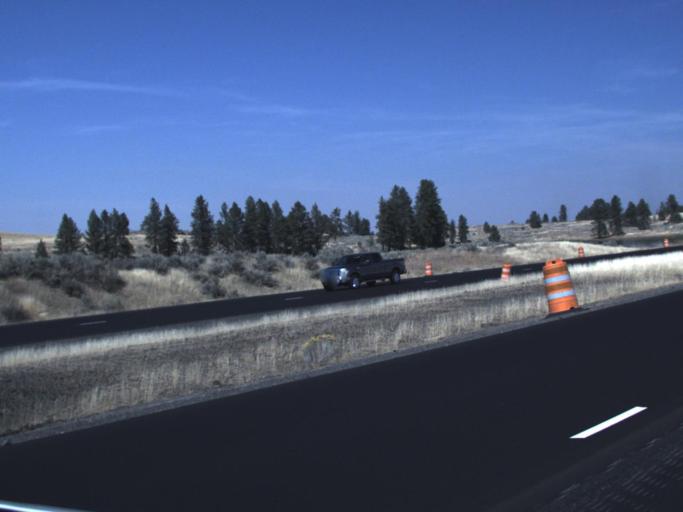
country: US
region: Washington
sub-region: Spokane County
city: Medical Lake
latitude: 47.3774
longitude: -117.8696
